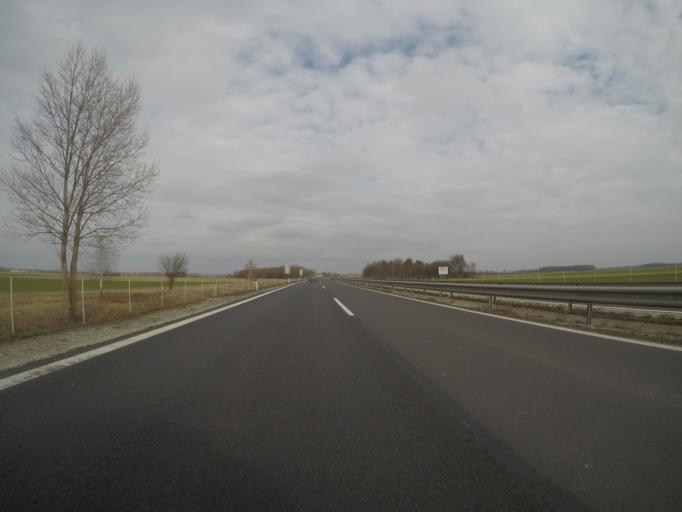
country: SI
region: Murska Sobota
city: Krog
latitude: 46.6311
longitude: 16.1464
